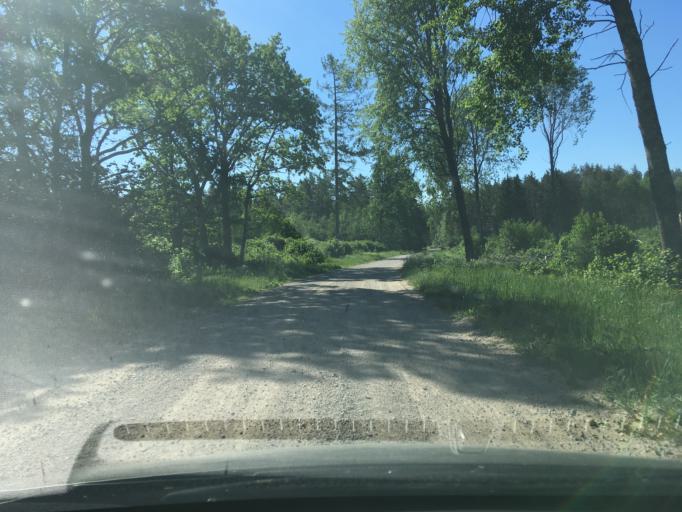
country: EE
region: Laeaene
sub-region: Lihula vald
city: Lihula
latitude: 58.6416
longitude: 23.7893
